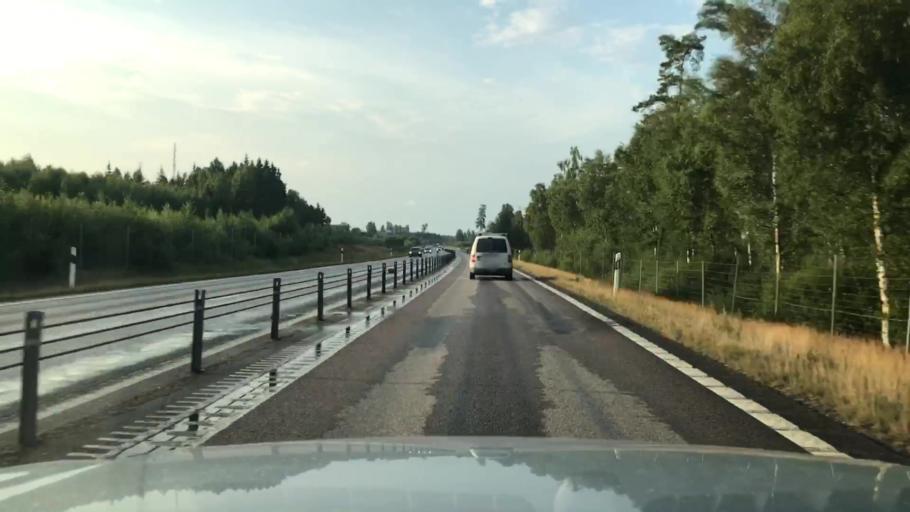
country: SE
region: Kronoberg
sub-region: Ljungby Kommun
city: Lagan
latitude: 56.9107
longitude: 13.9715
